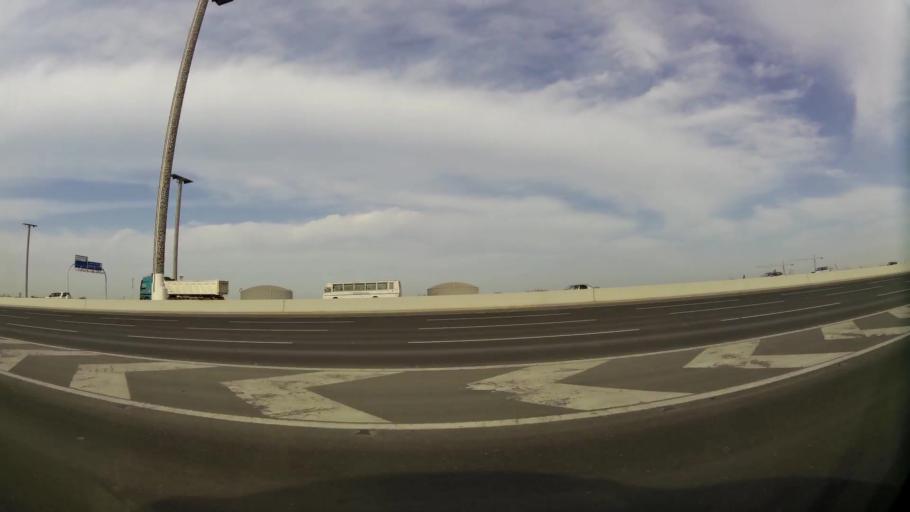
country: QA
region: Al Wakrah
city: Al Wakrah
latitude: 25.2345
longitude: 51.5927
